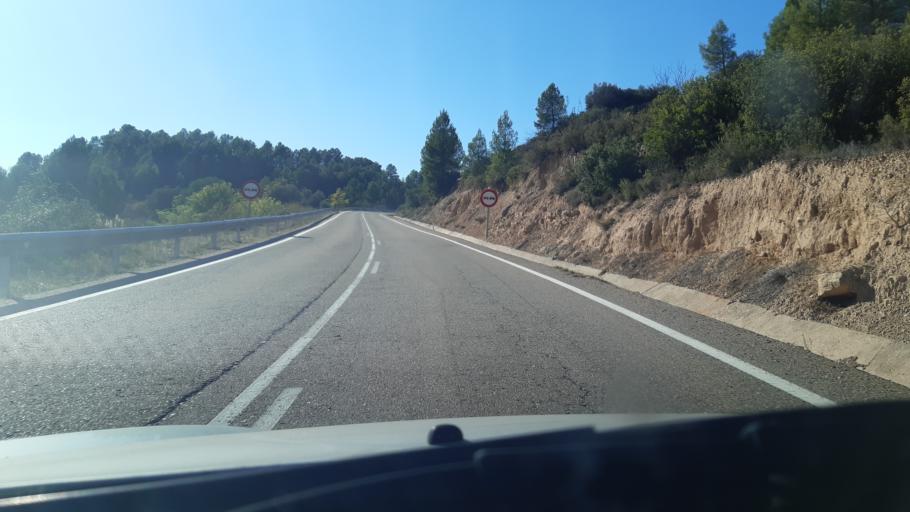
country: ES
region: Aragon
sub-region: Provincia de Teruel
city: Torre del Compte
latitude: 40.9057
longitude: 0.0960
